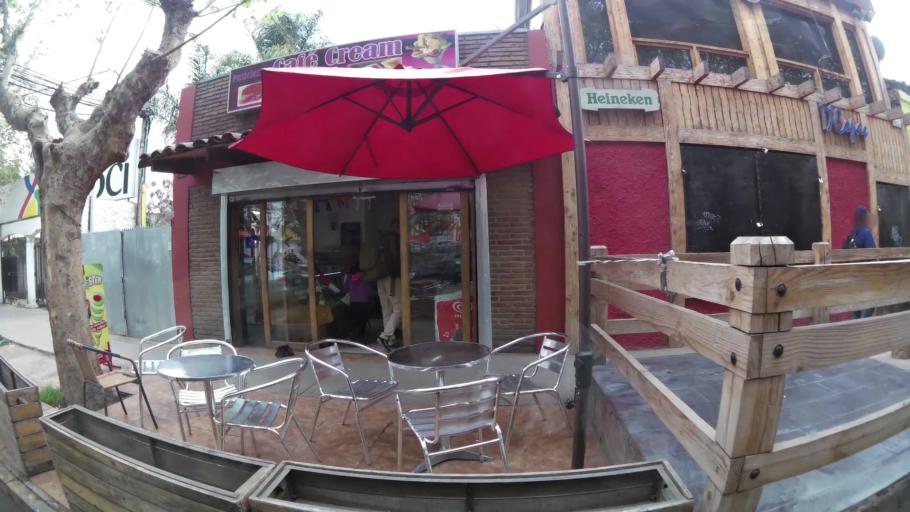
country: CL
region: Santiago Metropolitan
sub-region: Provincia de Chacabuco
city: Chicureo Abajo
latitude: -33.2030
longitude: -70.6754
